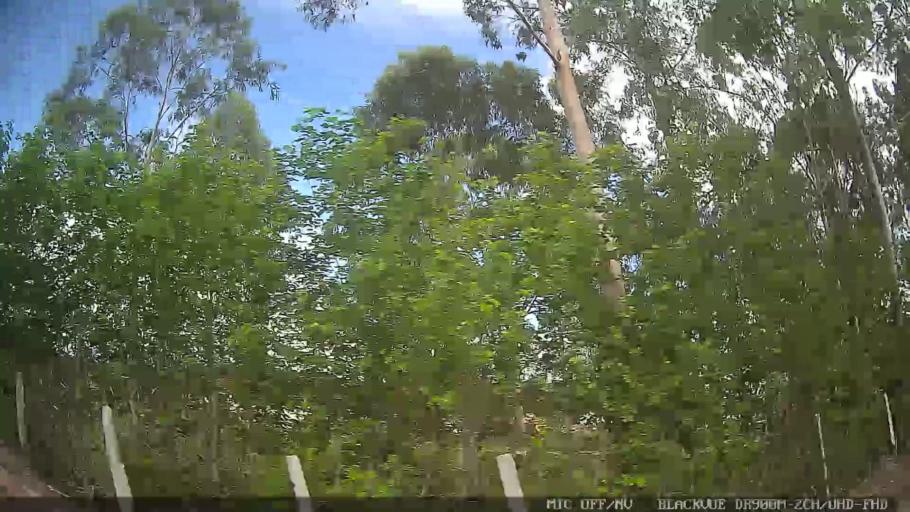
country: BR
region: Sao Paulo
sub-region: Conchas
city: Conchas
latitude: -22.9842
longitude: -47.9909
